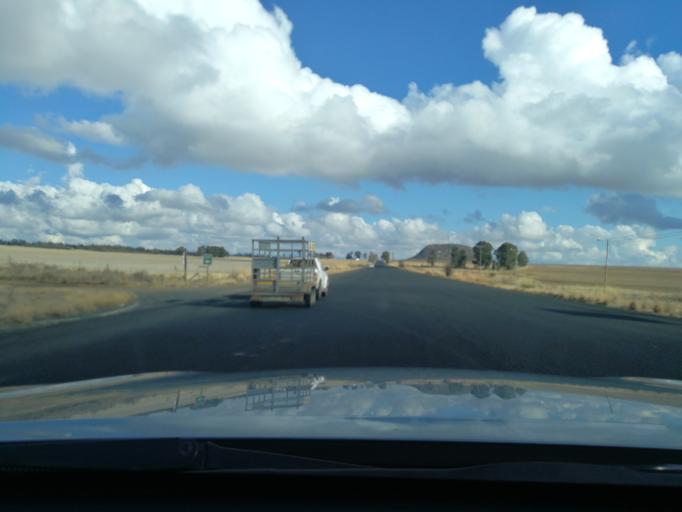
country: ZA
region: Orange Free State
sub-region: Thabo Mofutsanyana District Municipality
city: Reitz
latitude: -27.8829
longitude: 28.3989
